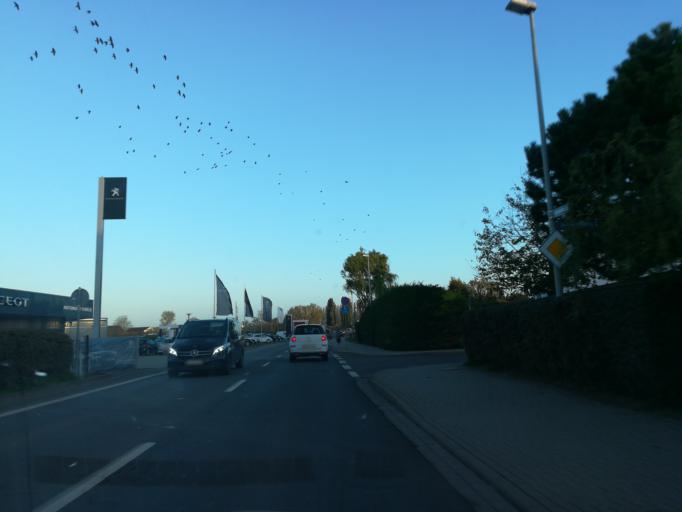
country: DE
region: Saxony-Anhalt
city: Diesdorf
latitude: 52.1338
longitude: 11.5732
